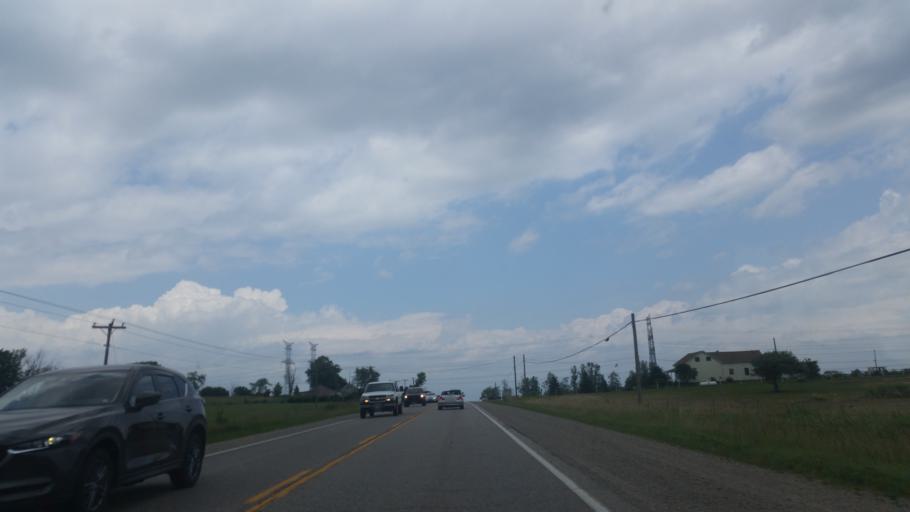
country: CA
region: Ontario
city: Orangeville
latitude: 43.7192
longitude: -80.1109
